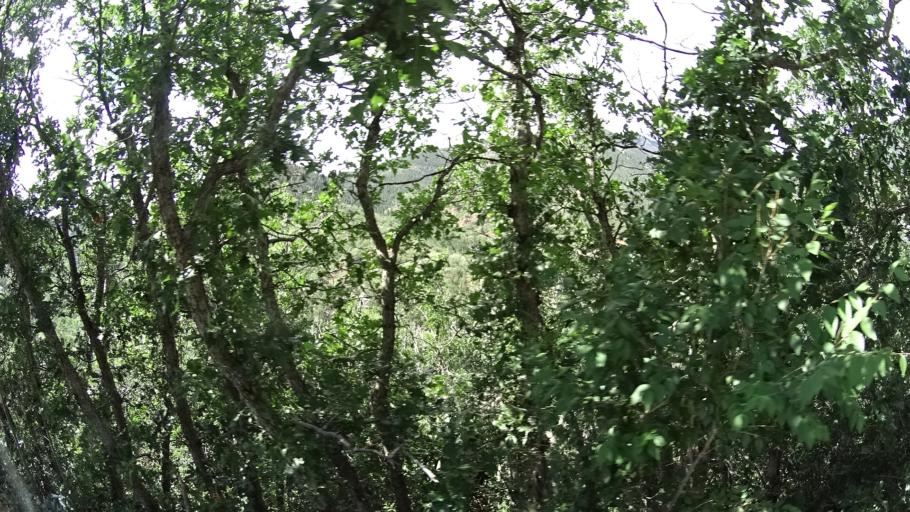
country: US
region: Colorado
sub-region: El Paso County
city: Manitou Springs
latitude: 38.8602
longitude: -104.9228
